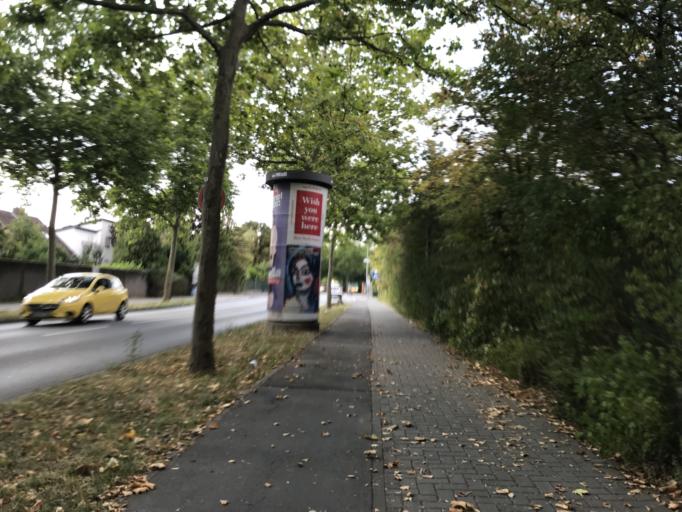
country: DE
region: Rheinland-Pfalz
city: Mainz
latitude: 50.0153
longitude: 8.2951
